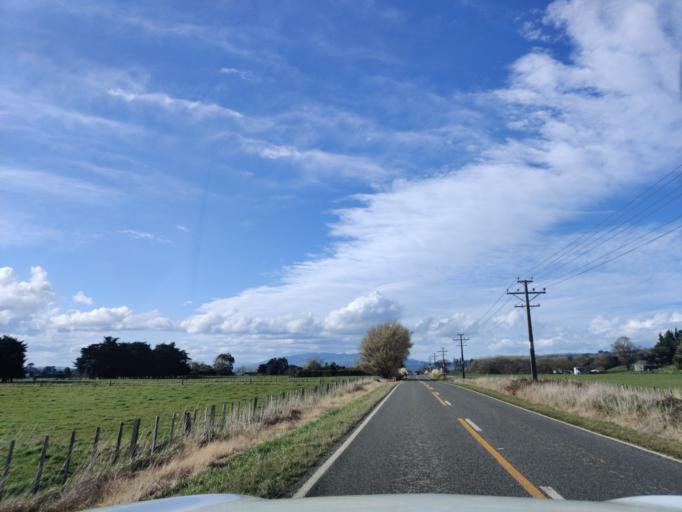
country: NZ
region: Manawatu-Wanganui
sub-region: Palmerston North City
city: Palmerston North
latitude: -40.3579
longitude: 175.6823
